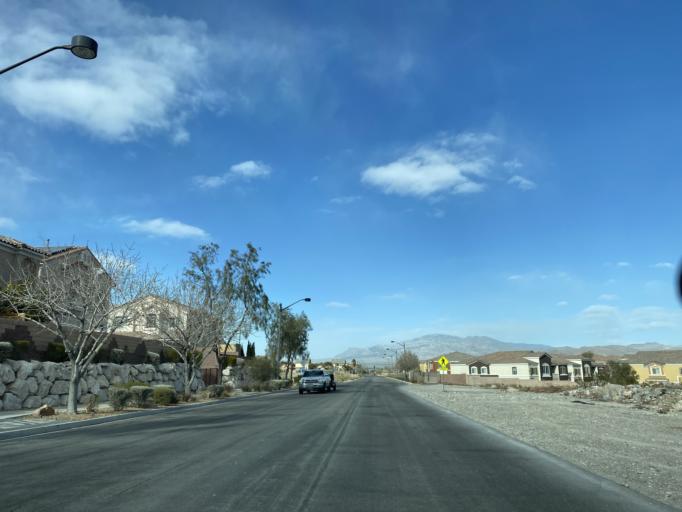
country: US
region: Nevada
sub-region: Clark County
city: Summerlin South
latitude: 36.3003
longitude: -115.3014
